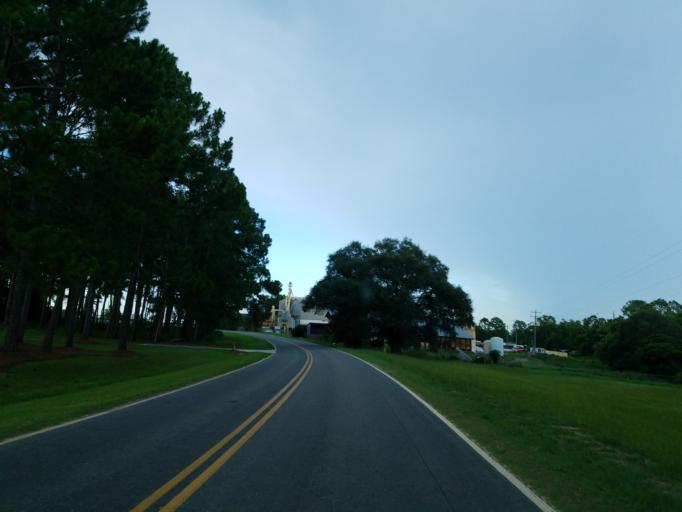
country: US
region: Georgia
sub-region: Cook County
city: Sparks
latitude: 31.2660
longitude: -83.4763
